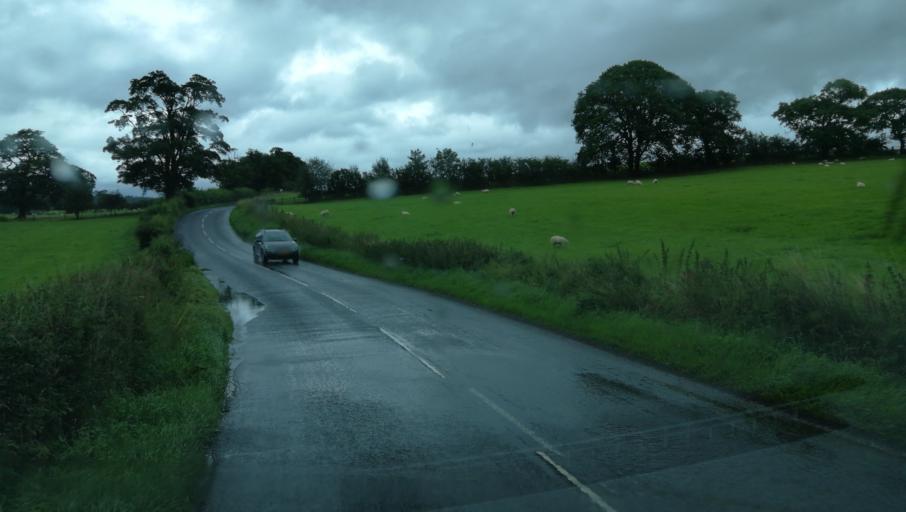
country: GB
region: England
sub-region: Cumbria
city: Penrith
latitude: 54.6182
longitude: -2.8269
